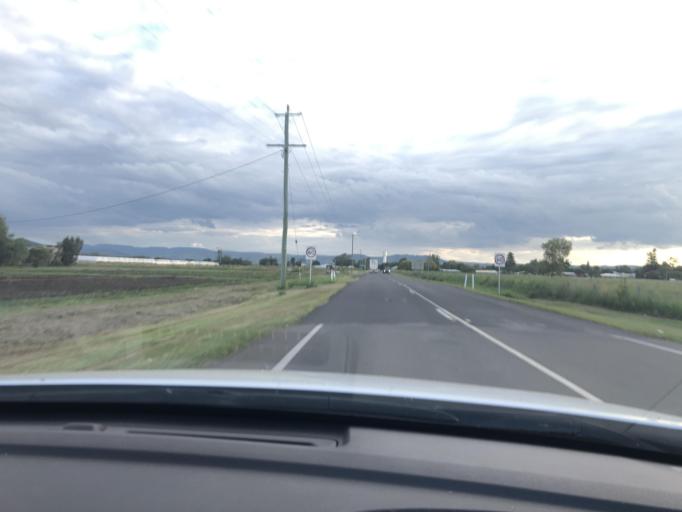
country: AU
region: Queensland
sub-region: Lockyer Valley
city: Gatton
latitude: -27.5847
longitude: 152.3630
